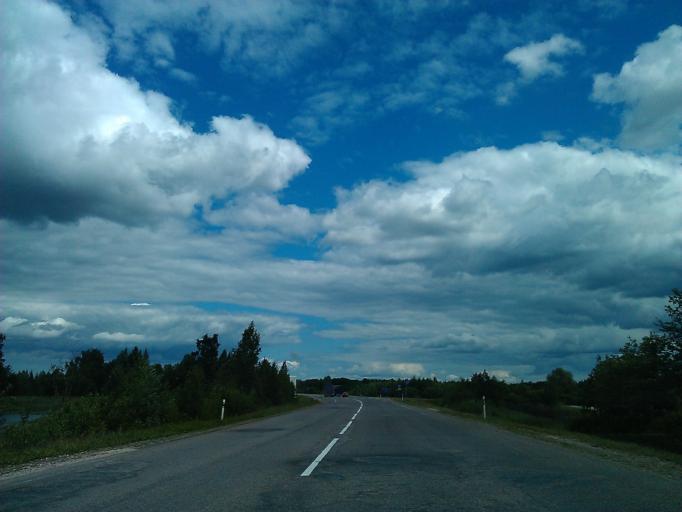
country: LV
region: Jelgava
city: Jelgava
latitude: 56.6342
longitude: 23.7660
